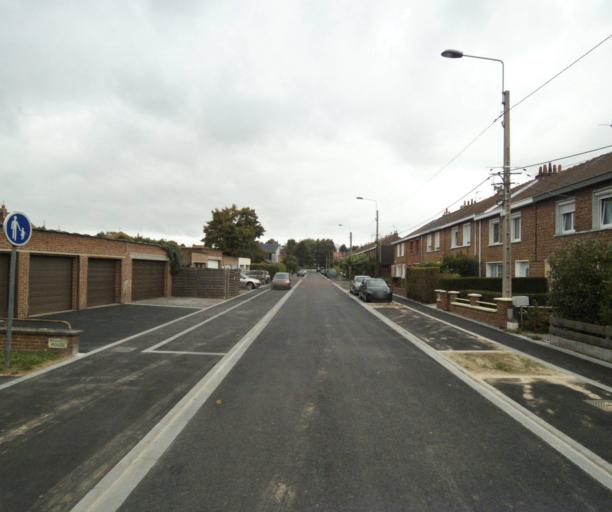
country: FR
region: Nord-Pas-de-Calais
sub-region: Departement du Nord
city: Lambersart
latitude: 50.6508
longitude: 3.0442
